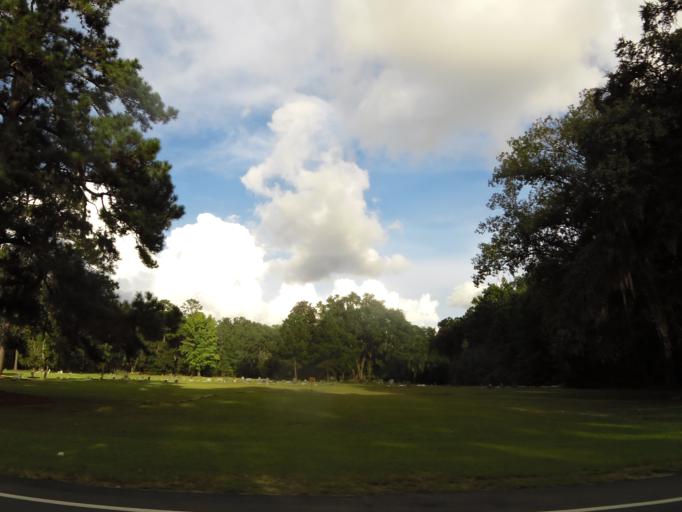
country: US
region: Georgia
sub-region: Liberty County
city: Midway
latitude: 31.8086
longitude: -81.4306
